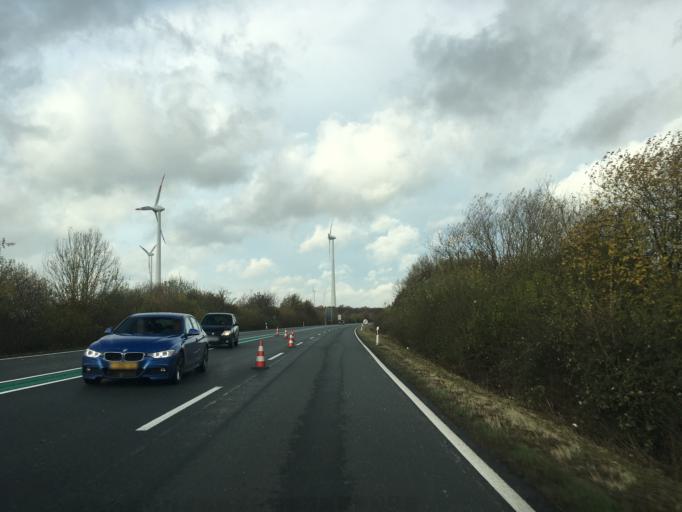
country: DE
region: North Rhine-Westphalia
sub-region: Regierungsbezirk Munster
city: Altenberge
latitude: 52.0768
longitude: 7.4244
